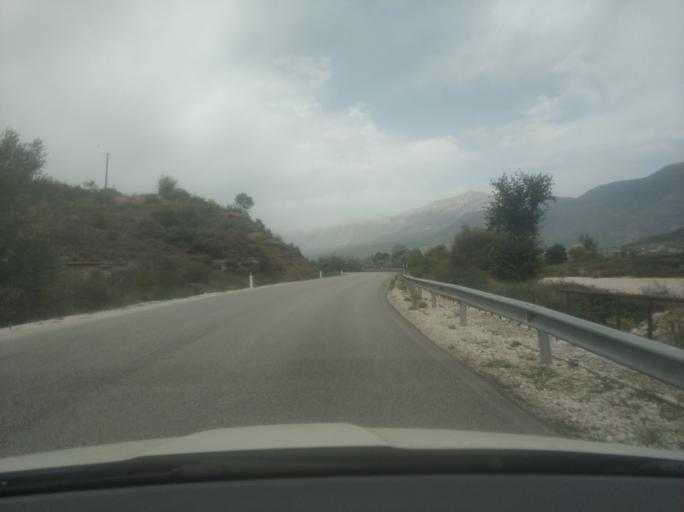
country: AL
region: Gjirokaster
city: Gjirokaster
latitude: 40.1075
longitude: 20.1225
